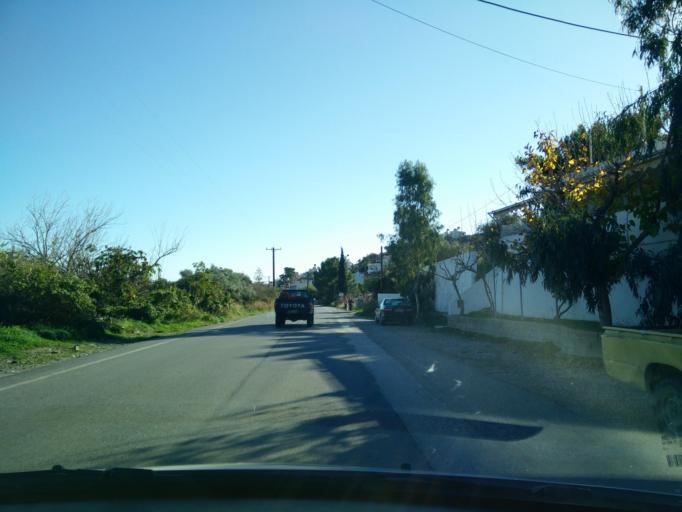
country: GR
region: Crete
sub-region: Nomos Lasithiou
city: Gra Liyia
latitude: 35.0082
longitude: 25.5836
